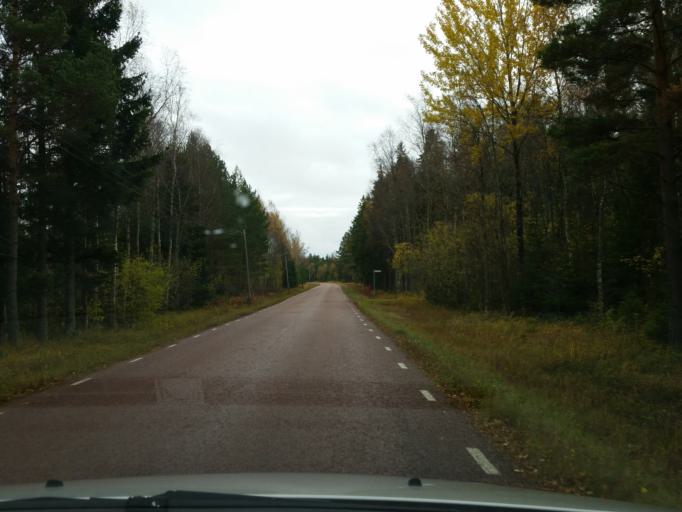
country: AX
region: Alands landsbygd
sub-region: Lemland
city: Lemland
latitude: 60.0021
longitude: 20.1868
